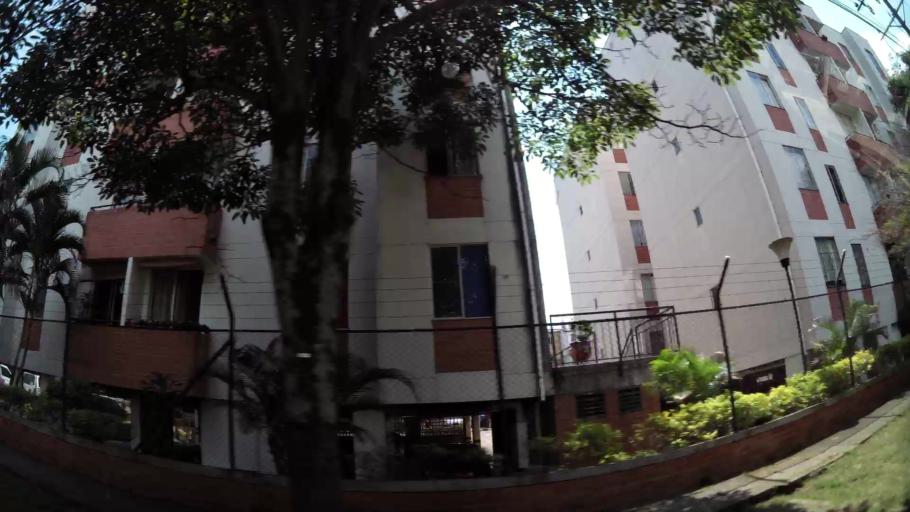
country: CO
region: Valle del Cauca
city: Cali
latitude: 3.4023
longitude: -76.5391
